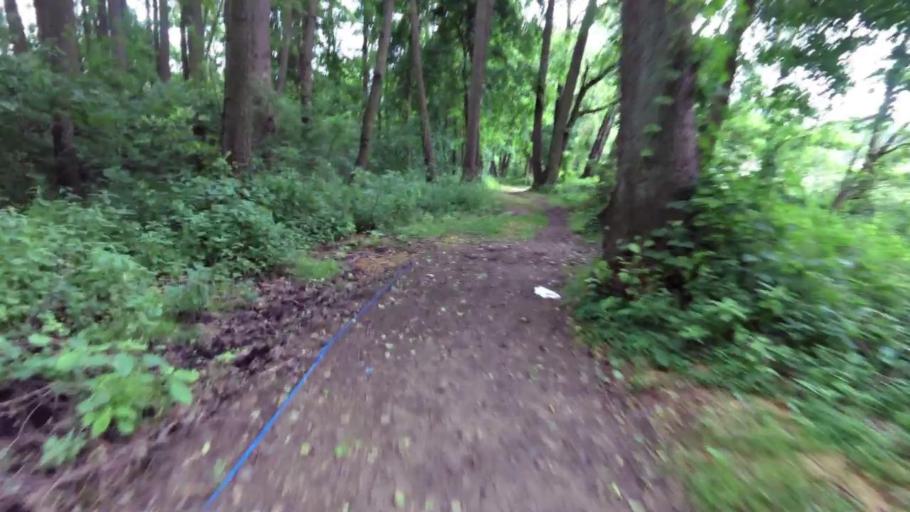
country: PL
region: West Pomeranian Voivodeship
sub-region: Powiat stargardzki
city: Chociwel
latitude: 53.4681
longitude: 15.3579
